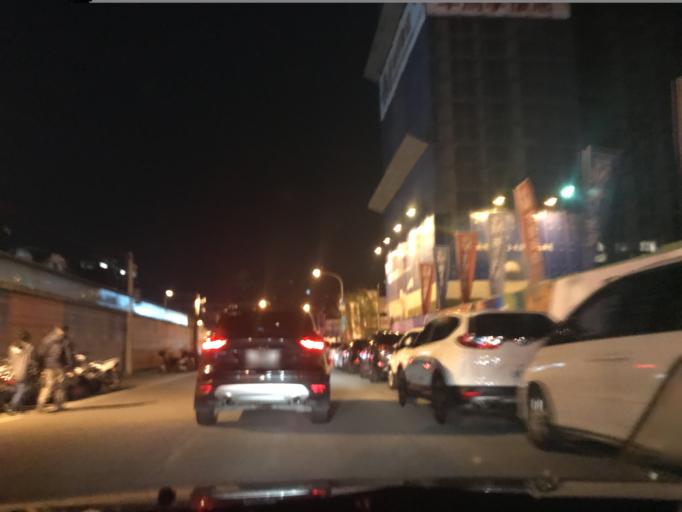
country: TW
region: Taiwan
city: Daxi
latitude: 24.9323
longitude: 121.2834
